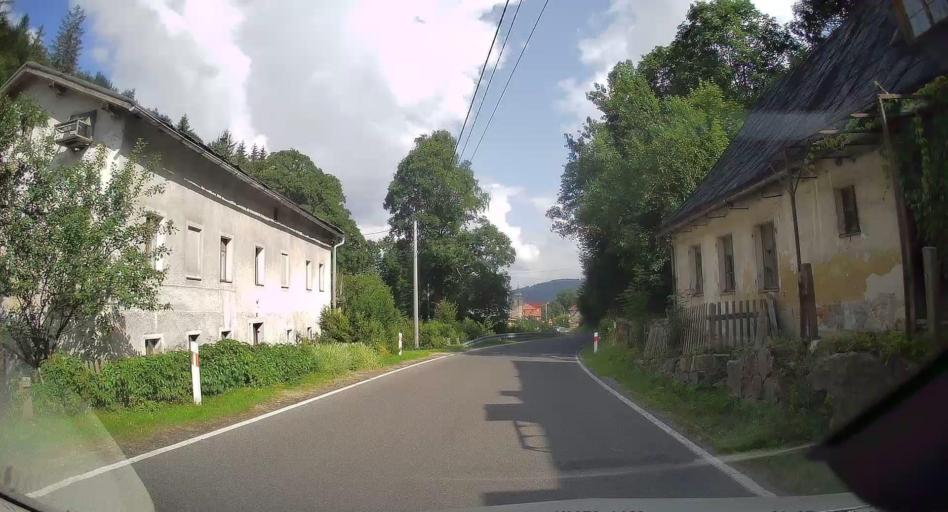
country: PL
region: Lower Silesian Voivodeship
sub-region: Powiat walbrzyski
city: Walim
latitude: 50.6918
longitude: 16.4457
